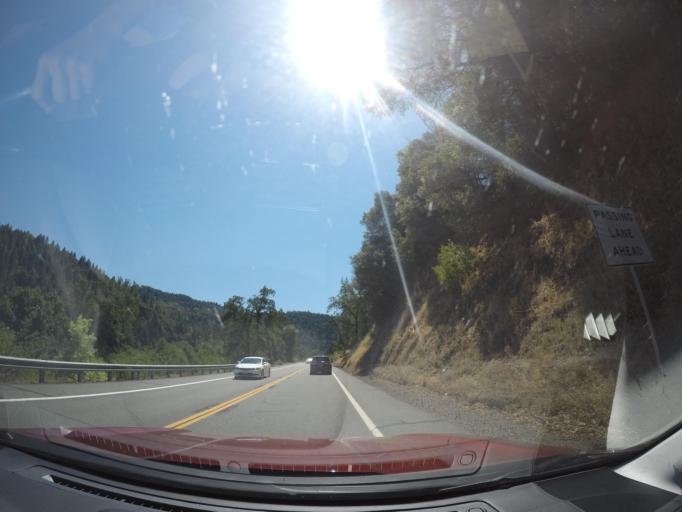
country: US
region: California
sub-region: Shasta County
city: Bella Vista
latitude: 40.7538
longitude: -122.0314
